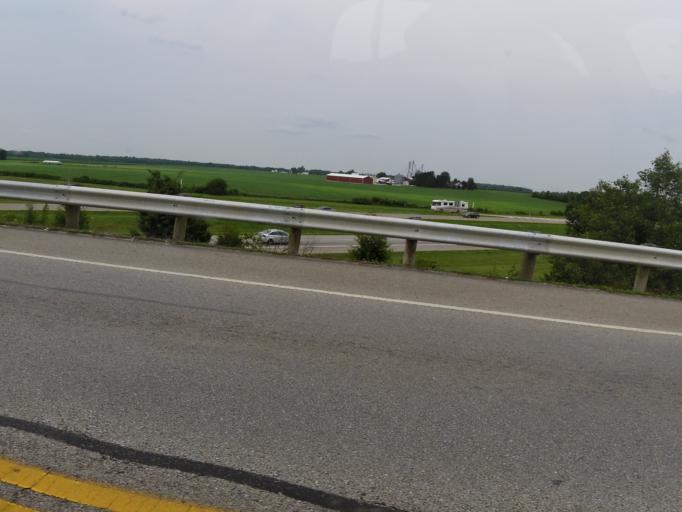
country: US
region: Ohio
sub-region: Clinton County
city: Wilmington
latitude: 39.4855
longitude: -83.9410
